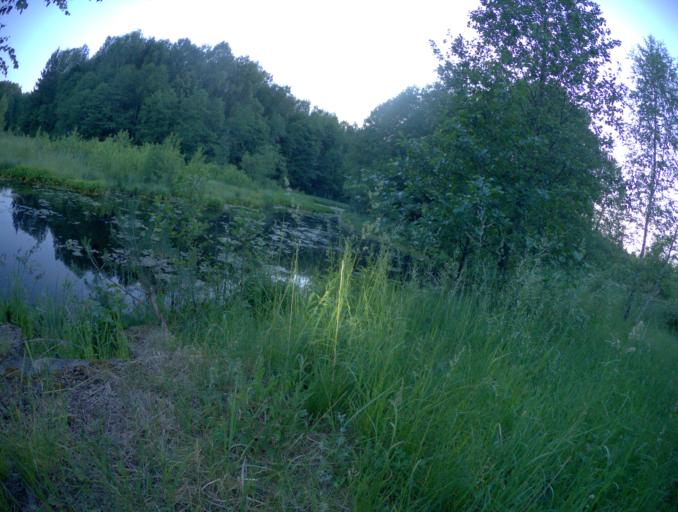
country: RU
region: Vladimir
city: Golovino
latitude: 56.0130
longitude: 40.4820
